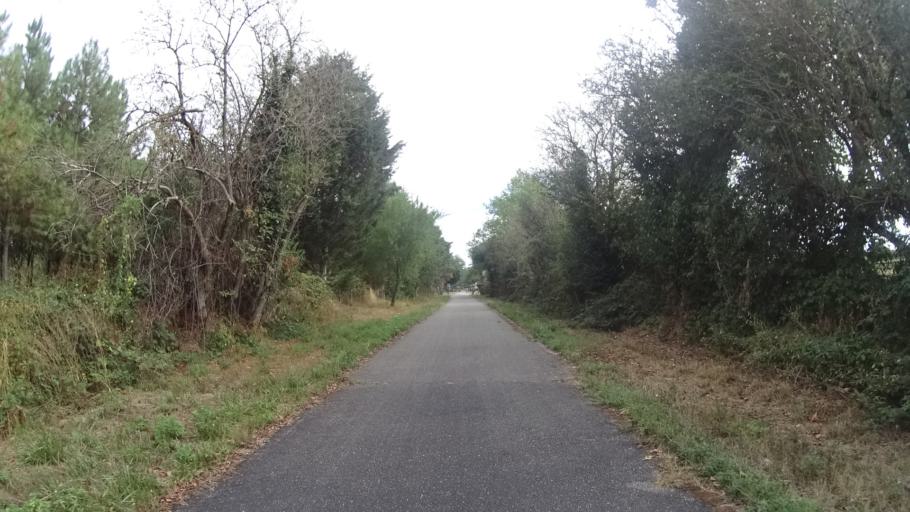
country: FR
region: Auvergne
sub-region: Departement de l'Allier
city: Diou
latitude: 46.5567
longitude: 3.7449
